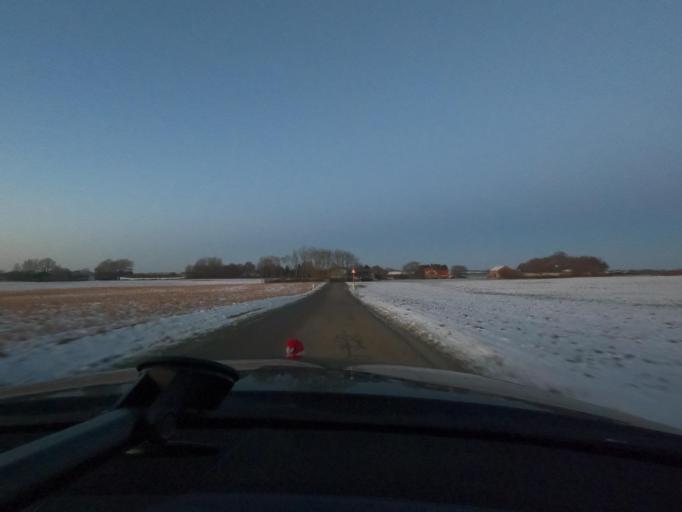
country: DK
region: South Denmark
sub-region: Sonderborg Kommune
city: Horuphav
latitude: 54.8650
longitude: 9.9488
